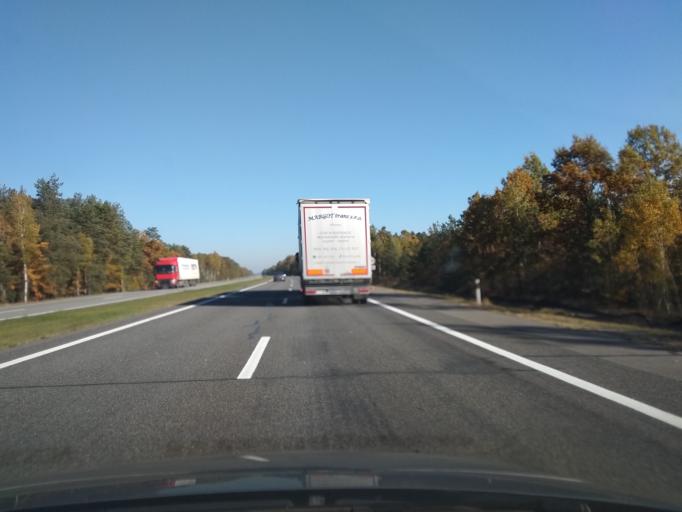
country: BY
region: Brest
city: Antopal'
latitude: 52.3676
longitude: 24.7375
